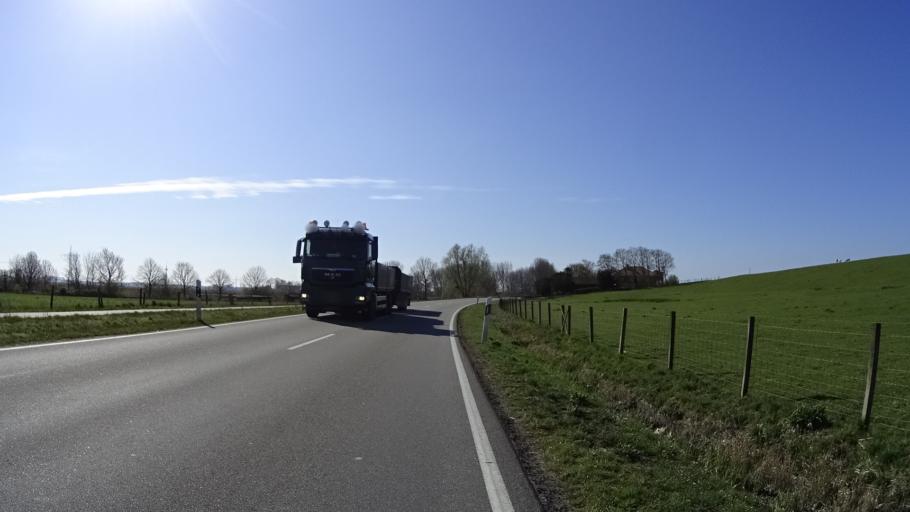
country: DE
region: Lower Saxony
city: Jemgum
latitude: 53.2873
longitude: 7.4048
